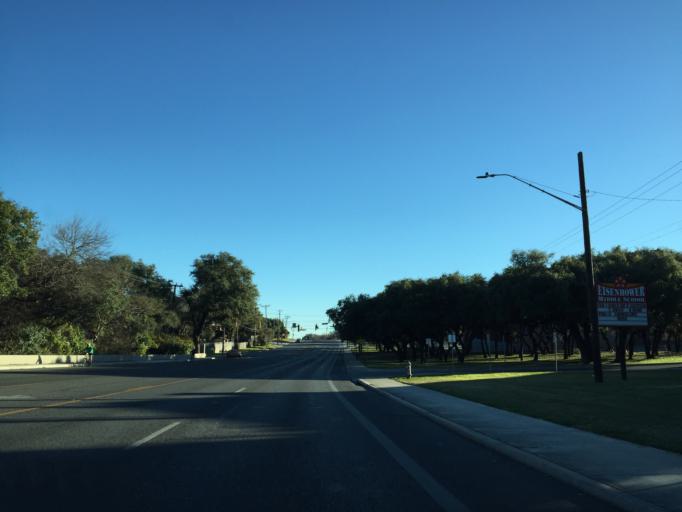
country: US
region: Texas
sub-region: Bexar County
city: Castle Hills
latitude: 29.5410
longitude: -98.5065
